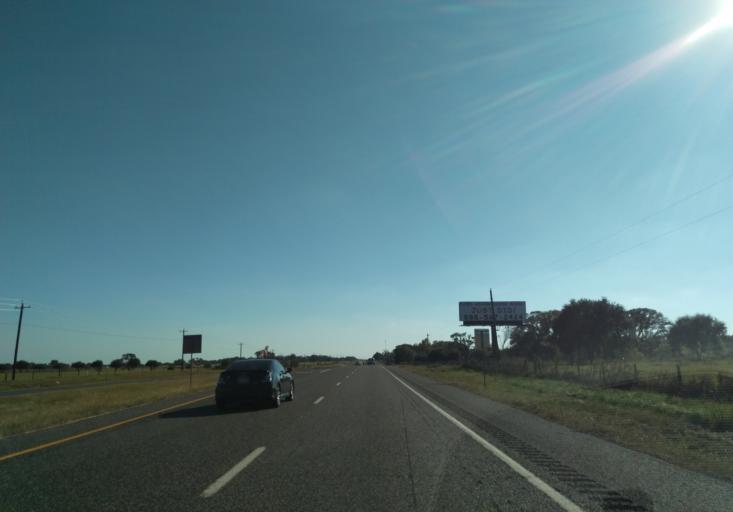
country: US
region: Texas
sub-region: Waller County
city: Hempstead
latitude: 30.1517
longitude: -96.0694
